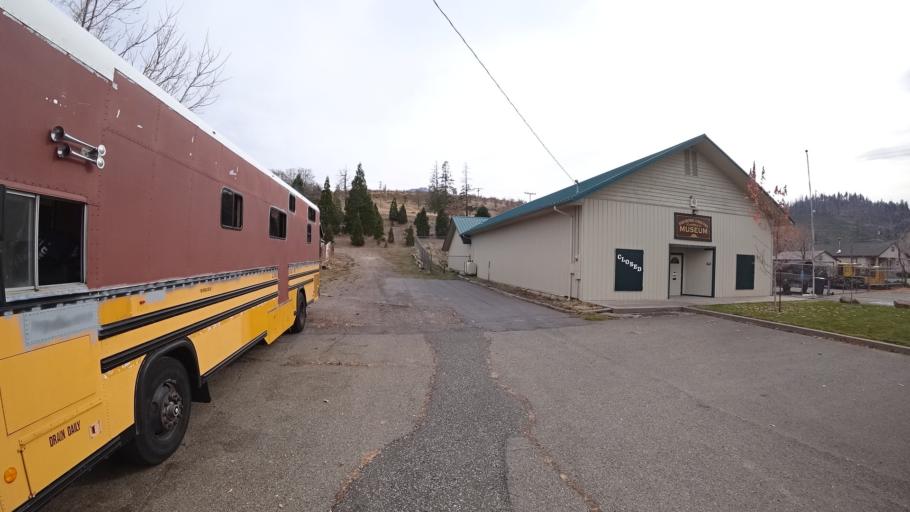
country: US
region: California
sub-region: Siskiyou County
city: Weed
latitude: 41.4255
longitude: -122.3836
